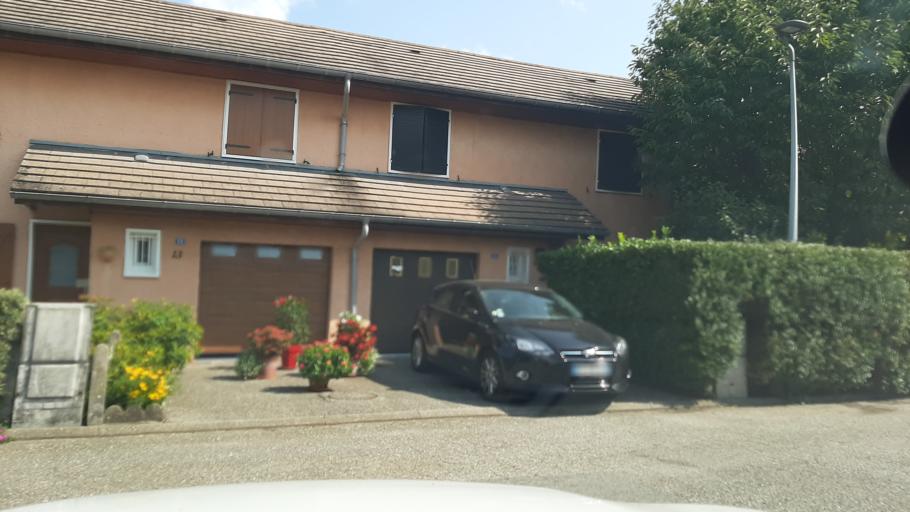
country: FR
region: Rhone-Alpes
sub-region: Departement de la Savoie
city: La Rochette
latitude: 45.4649
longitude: 6.1222
